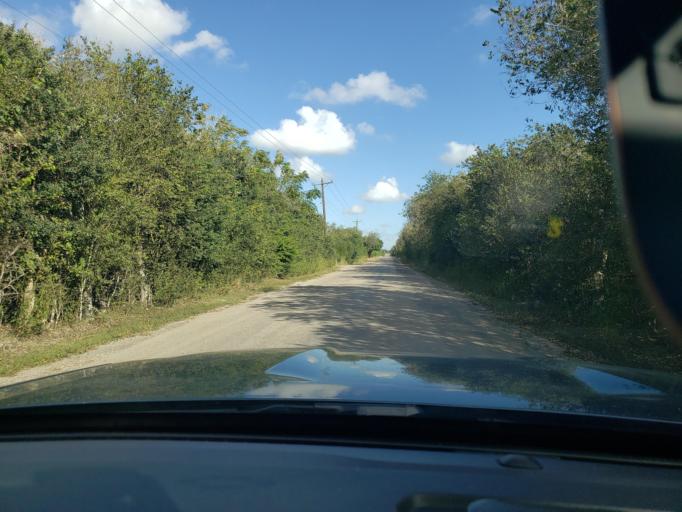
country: US
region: Texas
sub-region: Bee County
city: Beeville
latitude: 28.4503
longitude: -97.7172
